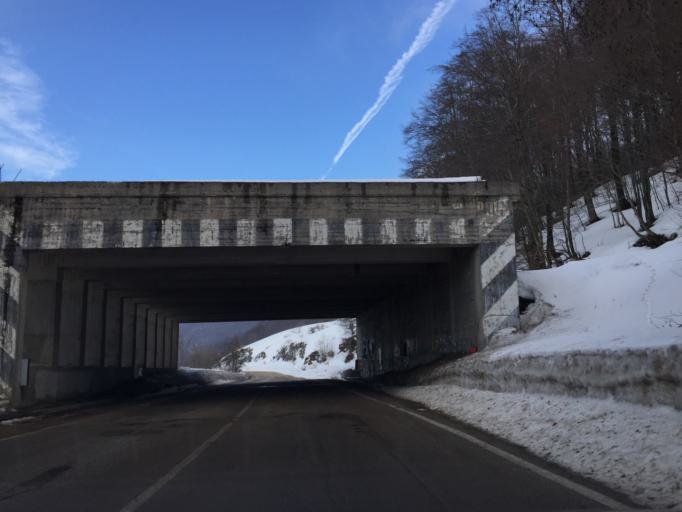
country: IT
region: Molise
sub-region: Provincia di Campobasso
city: San Massimo
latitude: 41.4656
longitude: 14.4104
